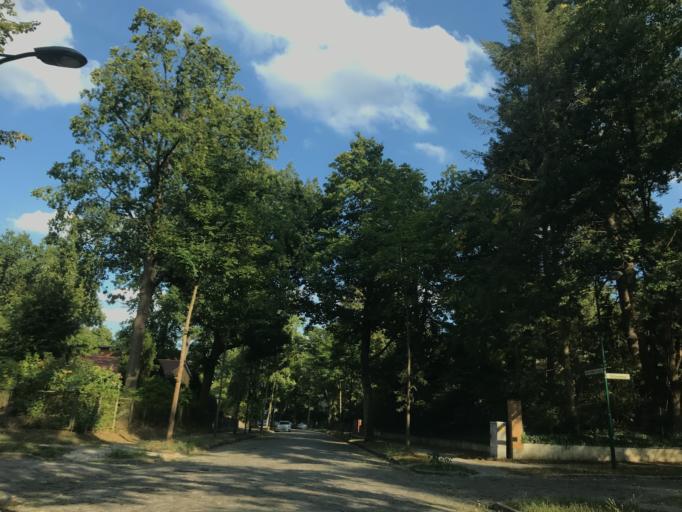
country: DE
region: Brandenburg
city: Teltow
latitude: 52.4100
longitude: 13.2448
